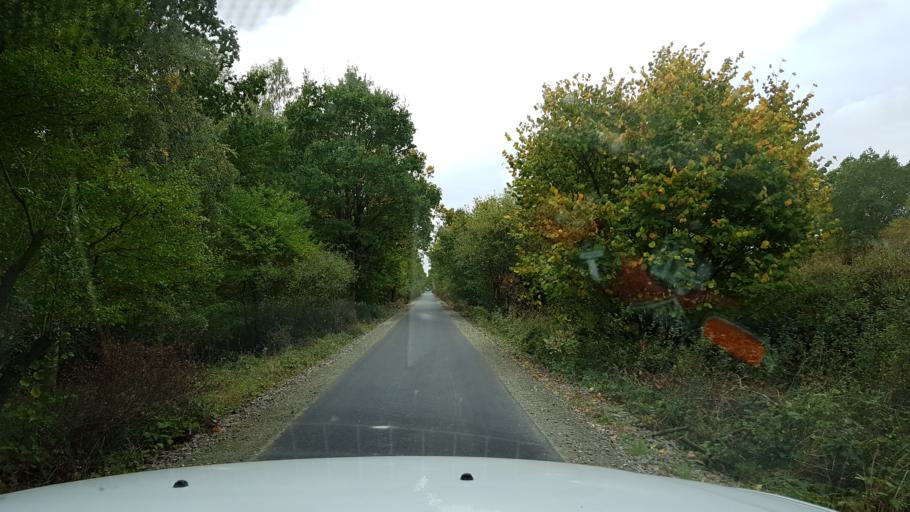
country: PL
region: West Pomeranian Voivodeship
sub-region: Powiat gryfinski
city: Moryn
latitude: 52.8828
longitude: 14.4288
